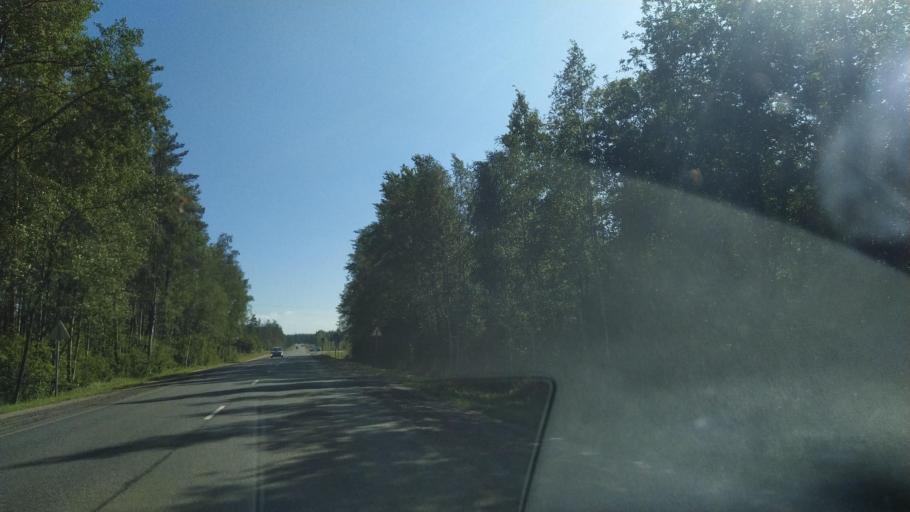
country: RU
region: Leningrad
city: Kirovsk
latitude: 59.9173
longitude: 30.9394
